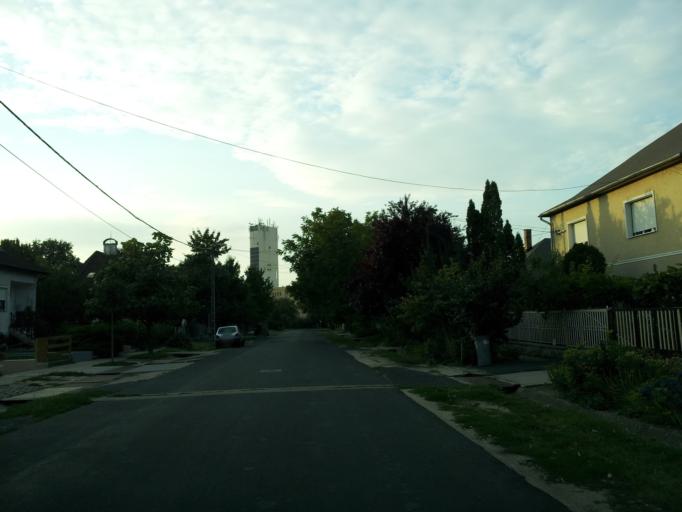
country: HU
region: Somogy
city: Siofok
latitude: 46.8984
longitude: 18.0446
